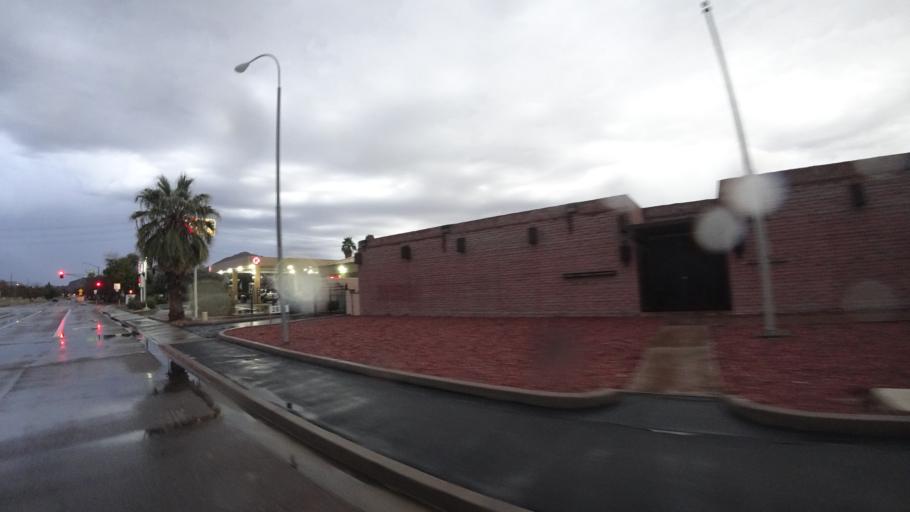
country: US
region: Arizona
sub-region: Maricopa County
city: Paradise Valley
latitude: 33.4793
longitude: -111.9780
